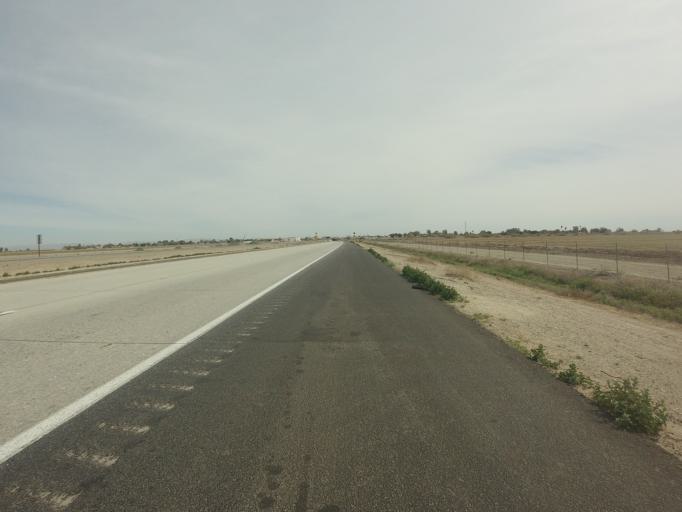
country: US
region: California
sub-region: Imperial County
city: Westmorland
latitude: 33.0370
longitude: -115.6373
